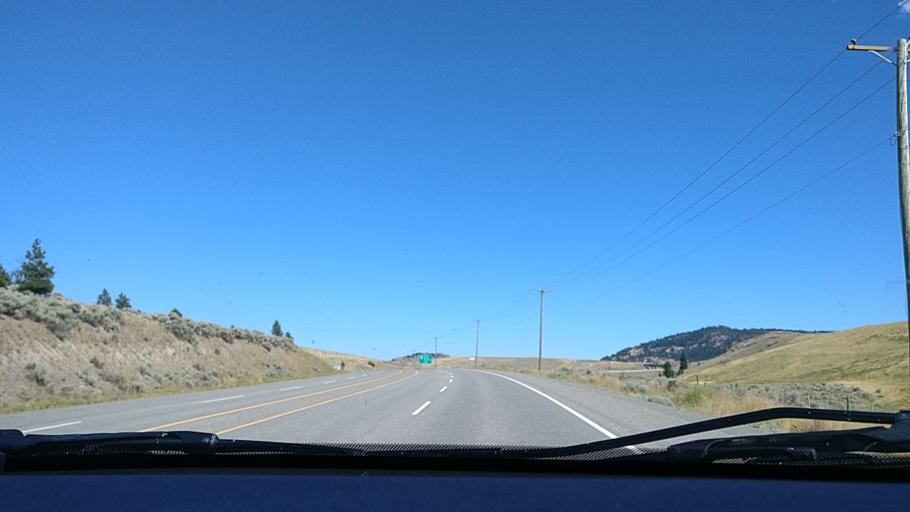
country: CA
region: British Columbia
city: Kamloops
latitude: 50.6688
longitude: -120.4755
